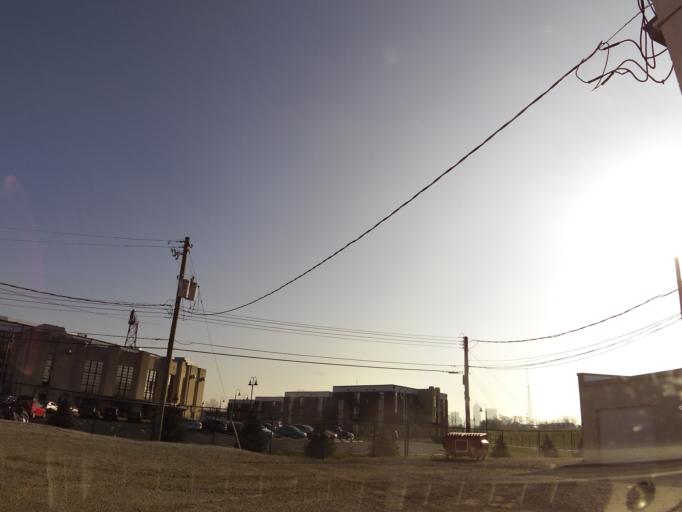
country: US
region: Indiana
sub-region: Marion County
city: Indianapolis
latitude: 39.7874
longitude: -86.1905
